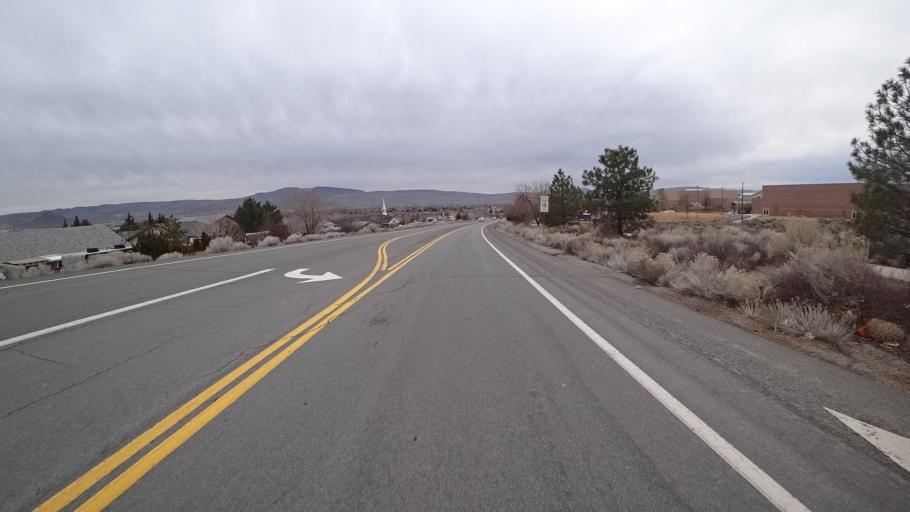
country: US
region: Nevada
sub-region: Washoe County
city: Spanish Springs
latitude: 39.6522
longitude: -119.7304
